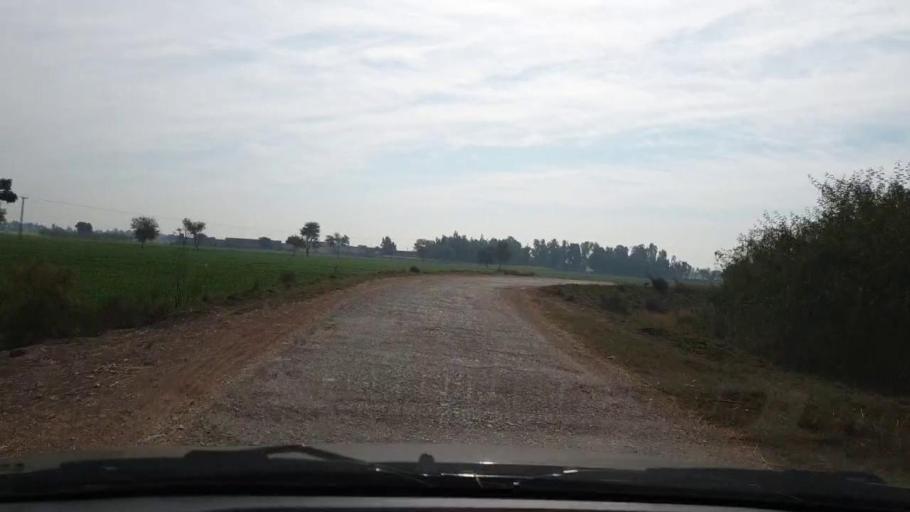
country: PK
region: Sindh
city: Shahpur Chakar
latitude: 26.1795
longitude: 68.6747
